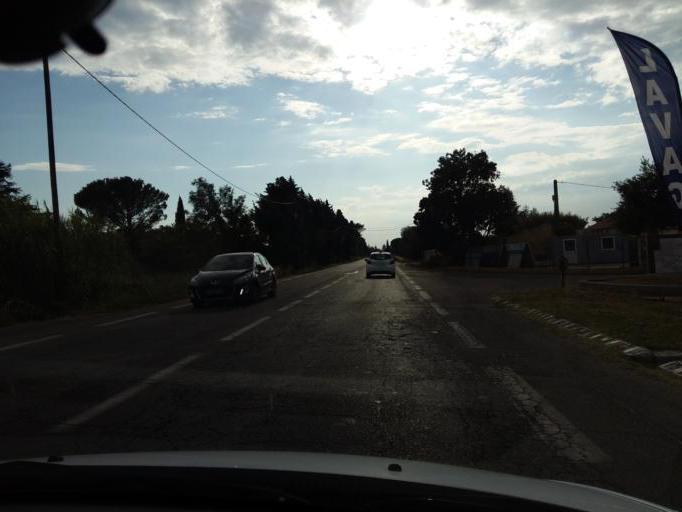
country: FR
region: Provence-Alpes-Cote d'Azur
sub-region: Departement du Vaucluse
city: Le Pontet
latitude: 43.9531
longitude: 4.8785
